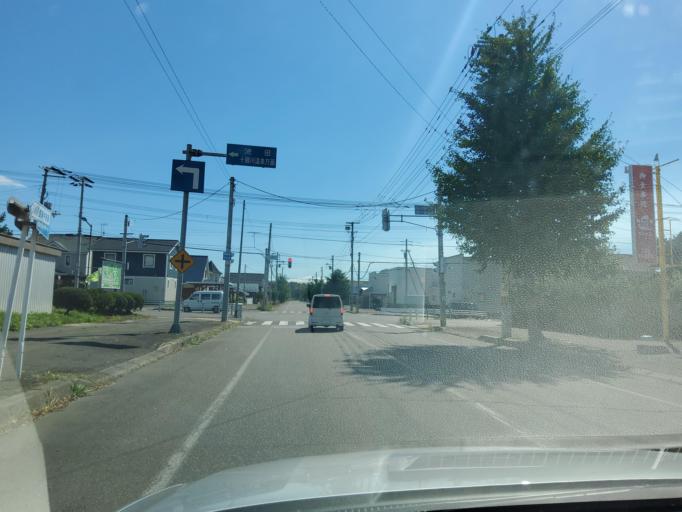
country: JP
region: Hokkaido
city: Obihiro
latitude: 42.9437
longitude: 143.2196
